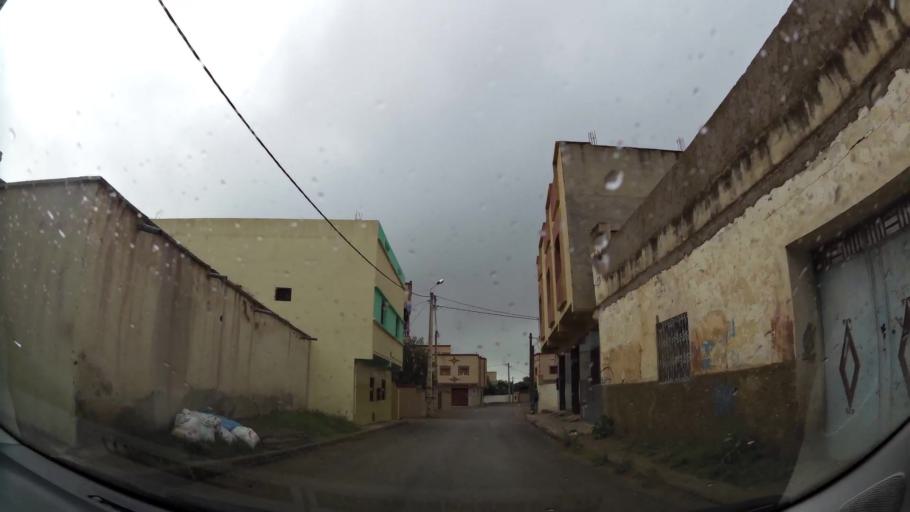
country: MA
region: Oriental
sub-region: Nador
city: Nador
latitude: 35.1548
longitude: -2.9601
